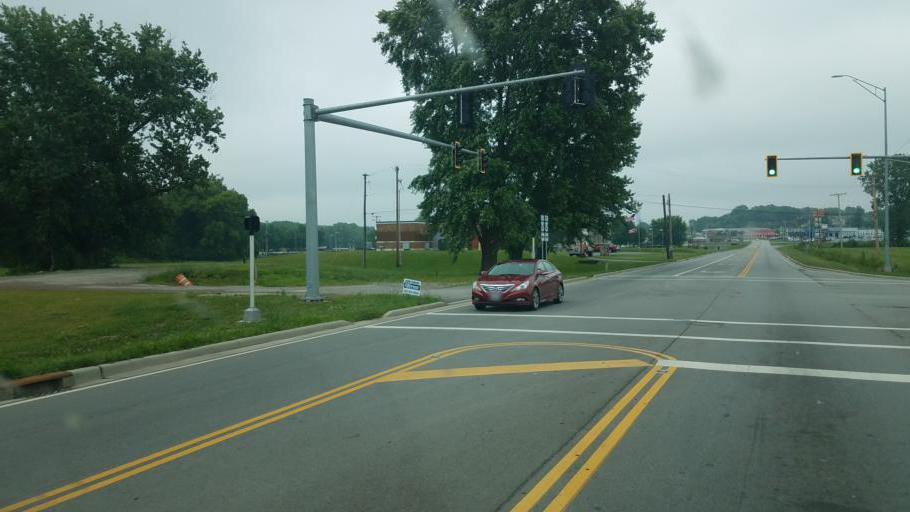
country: US
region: Ohio
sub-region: Highland County
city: Hillsboro
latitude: 39.2350
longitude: -83.6097
